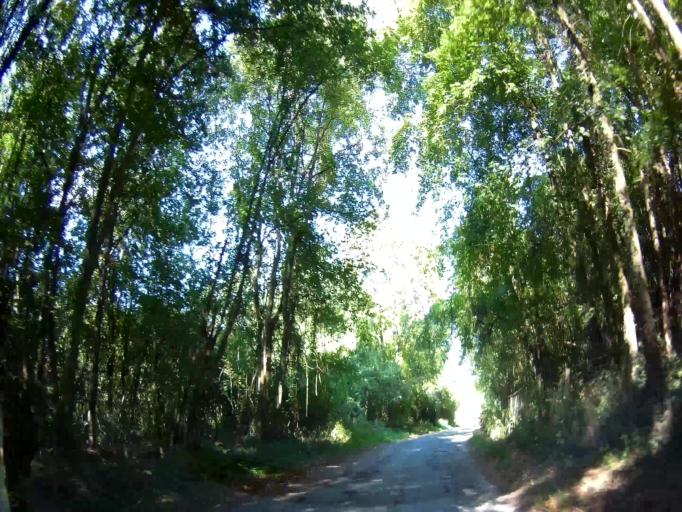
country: BE
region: Wallonia
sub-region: Province de Namur
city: Houyet
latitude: 50.2290
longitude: 4.9817
